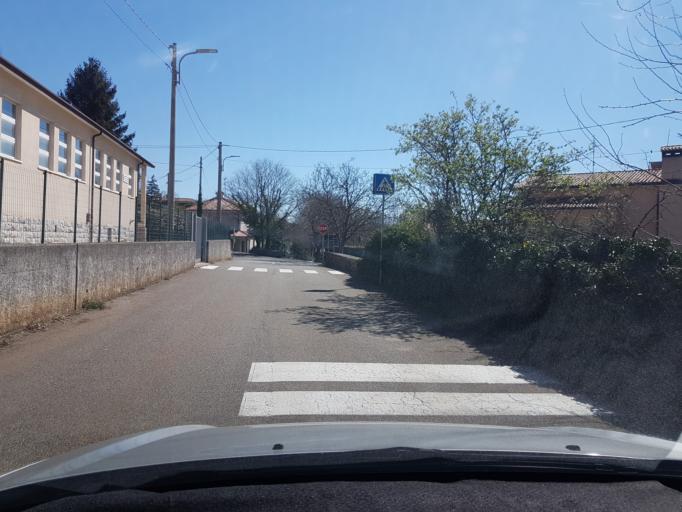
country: IT
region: Friuli Venezia Giulia
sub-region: Provincia di Trieste
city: Sgonico
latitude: 45.7483
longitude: 13.7276
